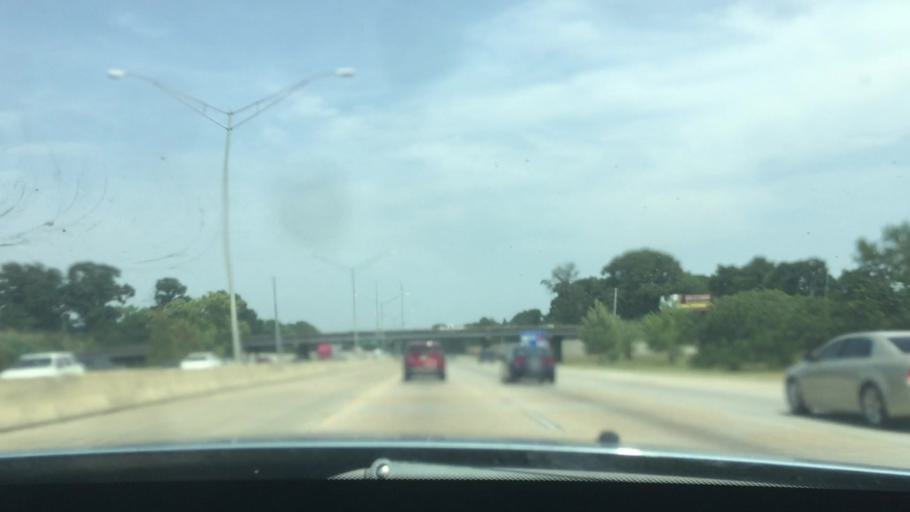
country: US
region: Louisiana
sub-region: East Baton Rouge Parish
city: Westminster
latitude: 30.4173
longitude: -91.0998
